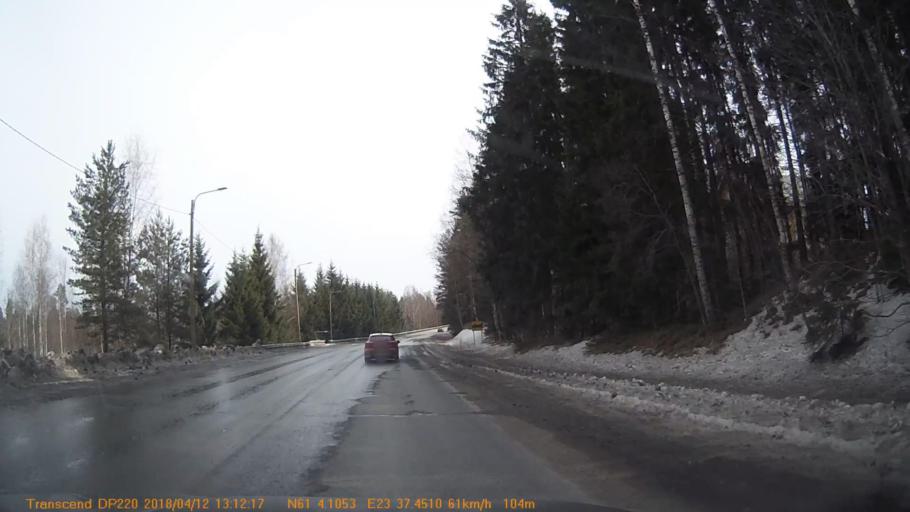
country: FI
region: Pirkanmaa
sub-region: Etelae-Pirkanmaa
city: Urjala
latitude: 61.0683
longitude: 23.6253
